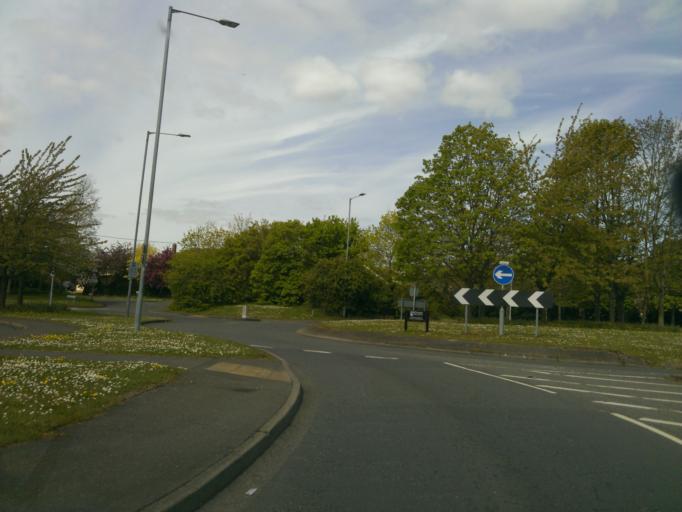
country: GB
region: England
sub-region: Essex
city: Eight Ash Green
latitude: 51.8935
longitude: 0.8253
